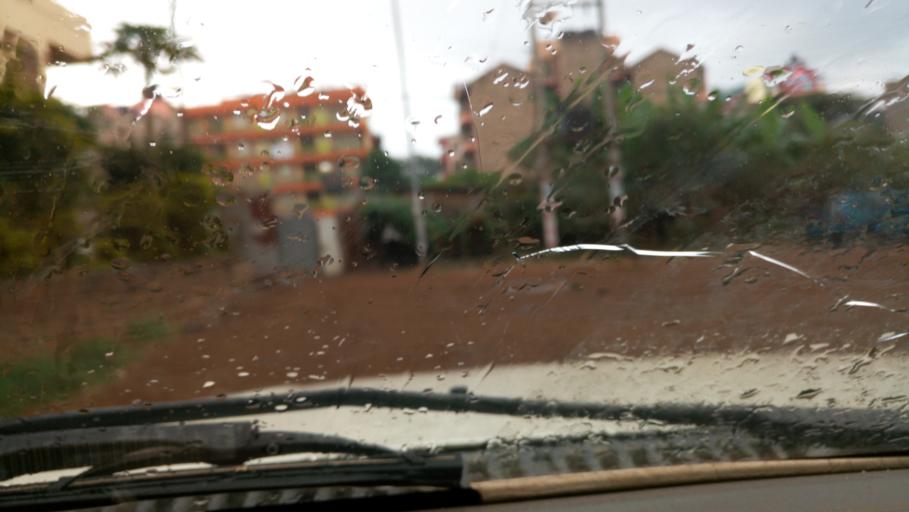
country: KE
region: Kiambu
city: Kiambu
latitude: -1.2171
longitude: 36.8880
